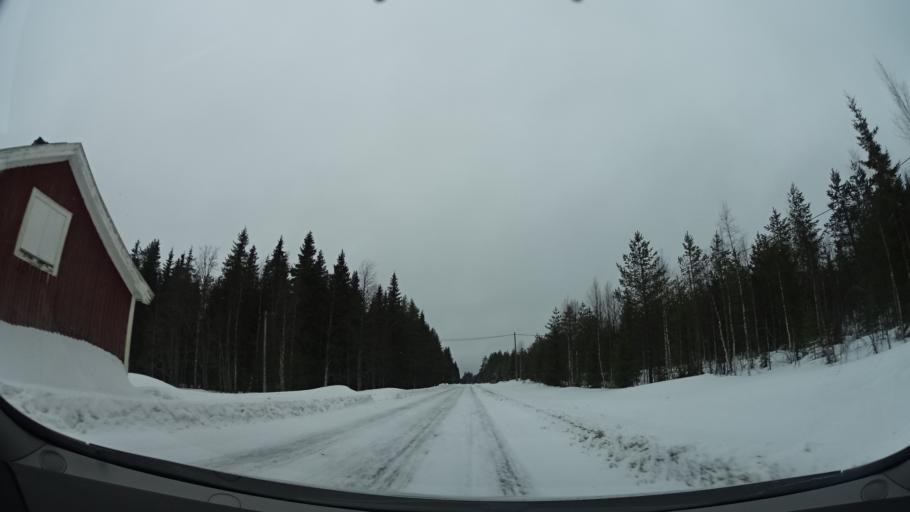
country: SE
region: Vaesterbotten
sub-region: Mala Kommun
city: Mala
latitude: 65.0954
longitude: 18.9287
